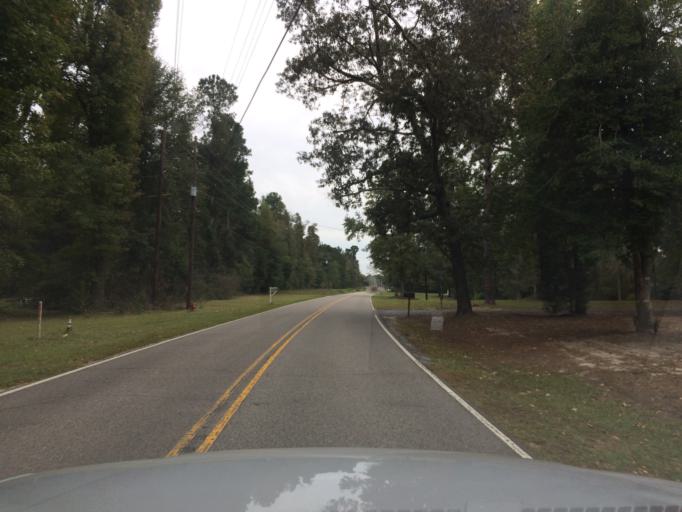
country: US
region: South Carolina
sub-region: Aiken County
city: New Ellenton
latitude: 33.4042
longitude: -81.6993
